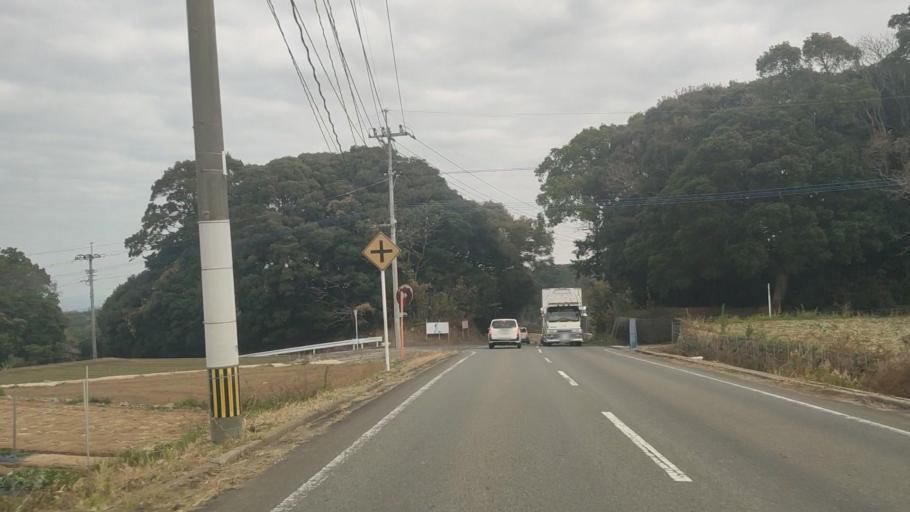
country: JP
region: Nagasaki
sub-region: Isahaya-shi
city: Isahaya
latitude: 32.8209
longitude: 130.1877
